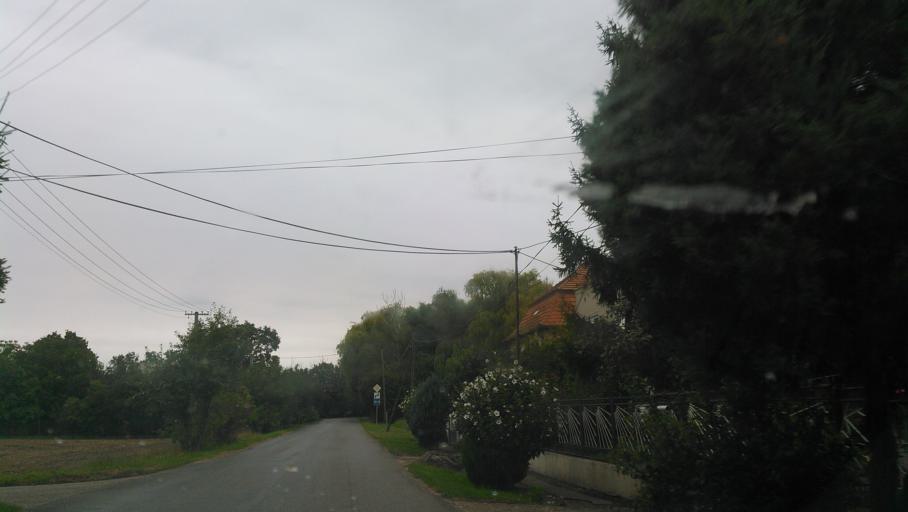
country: SK
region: Nitriansky
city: Kolarovo
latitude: 47.8868
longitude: 17.8987
